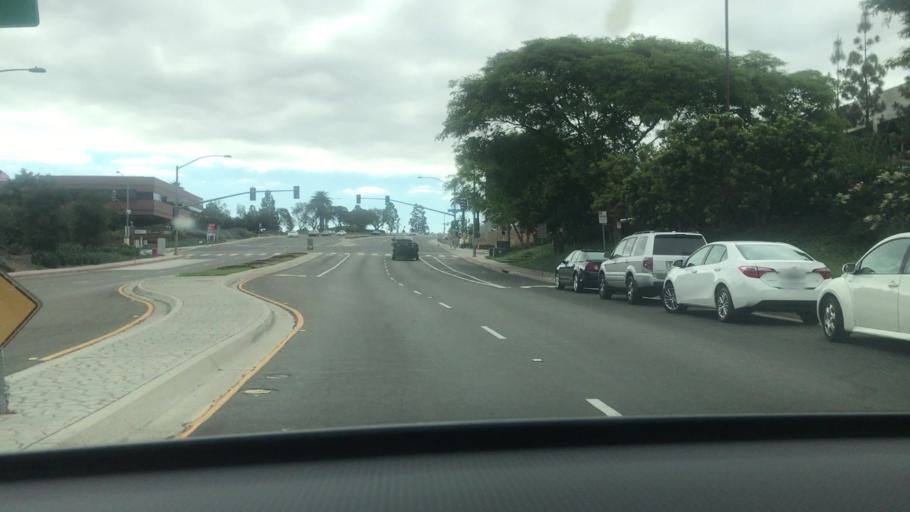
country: US
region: California
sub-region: San Diego County
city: Fairbanks Ranch
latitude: 32.9013
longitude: -117.1928
